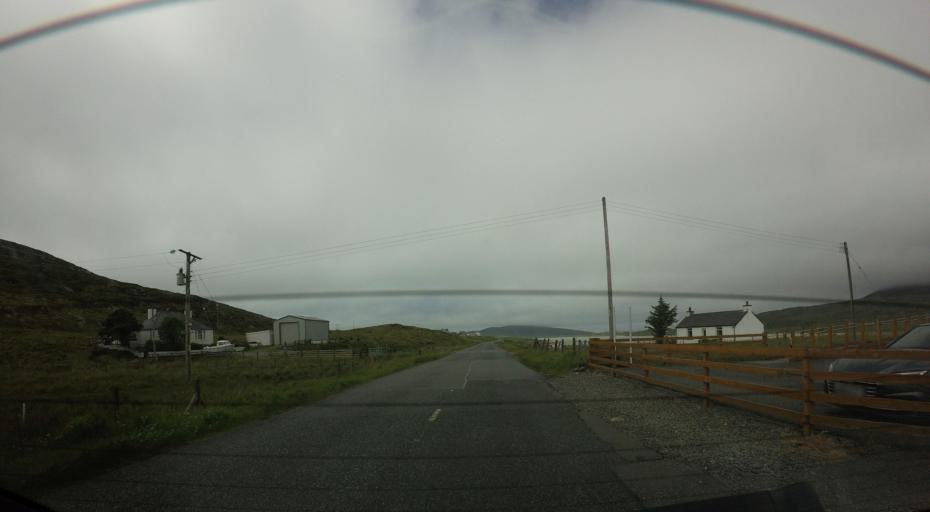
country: GB
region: Scotland
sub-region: Eilean Siar
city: Harris
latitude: 57.8664
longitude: -6.9263
